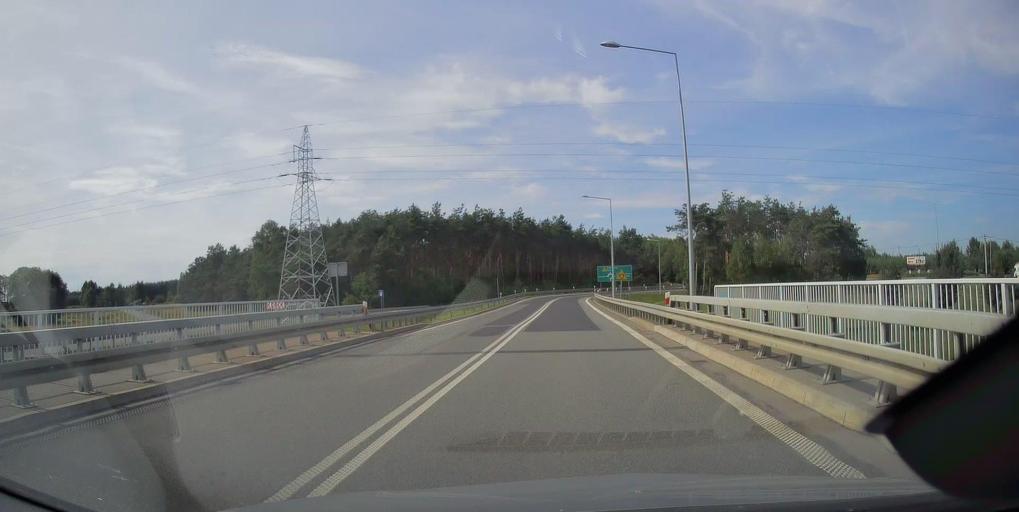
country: PL
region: Lodz Voivodeship
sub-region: Powiat tomaszowski
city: Tomaszow Mazowiecki
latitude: 51.5509
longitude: 19.9863
